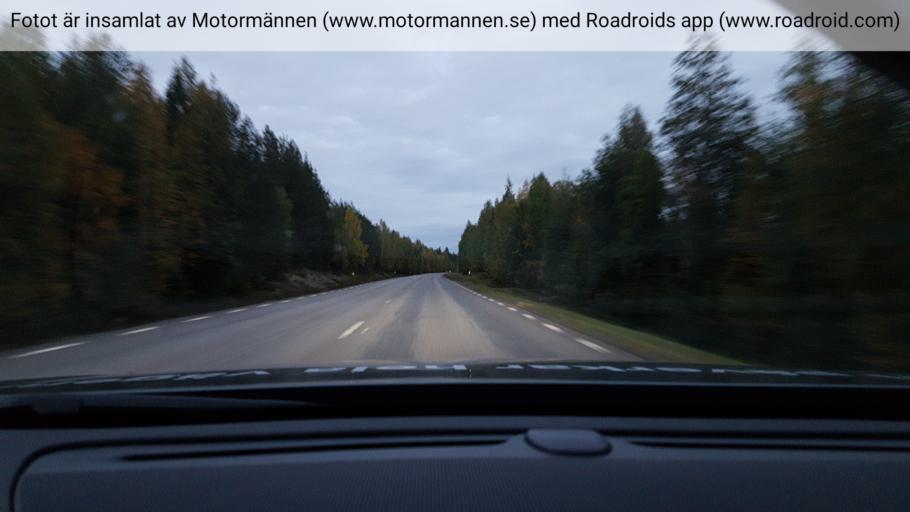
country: SE
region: Norrbotten
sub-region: Alvsbyns Kommun
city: AElvsbyn
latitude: 65.7807
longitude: 20.8200
